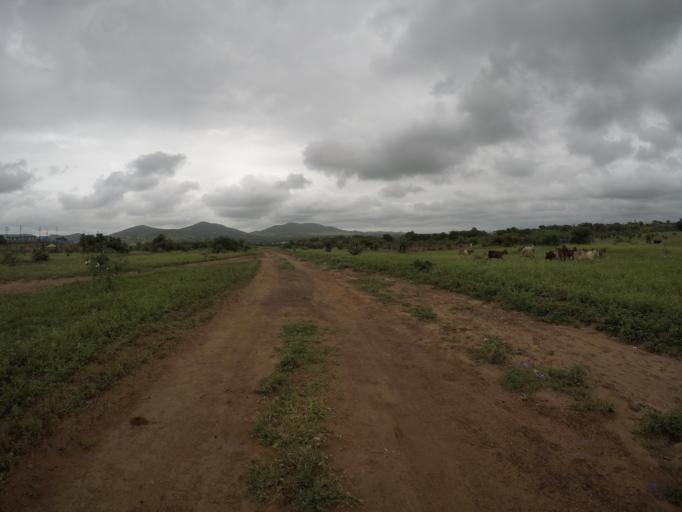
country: ZA
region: KwaZulu-Natal
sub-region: uThungulu District Municipality
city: Empangeni
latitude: -28.6068
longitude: 31.8654
